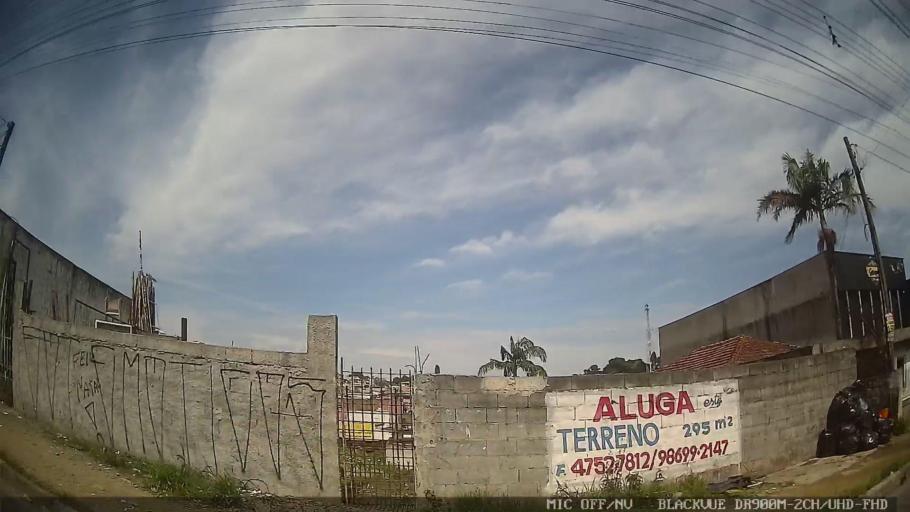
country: BR
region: Sao Paulo
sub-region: Suzano
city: Suzano
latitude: -23.5036
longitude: -46.3000
